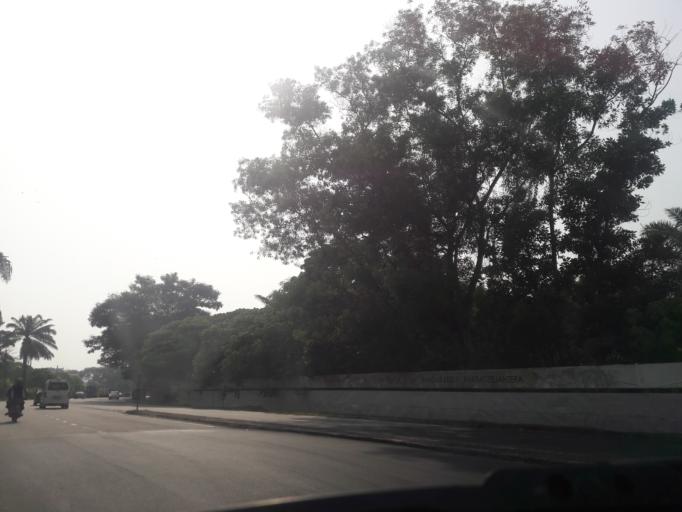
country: MY
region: Kedah
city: Kulim
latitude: 5.3460
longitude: 100.5199
